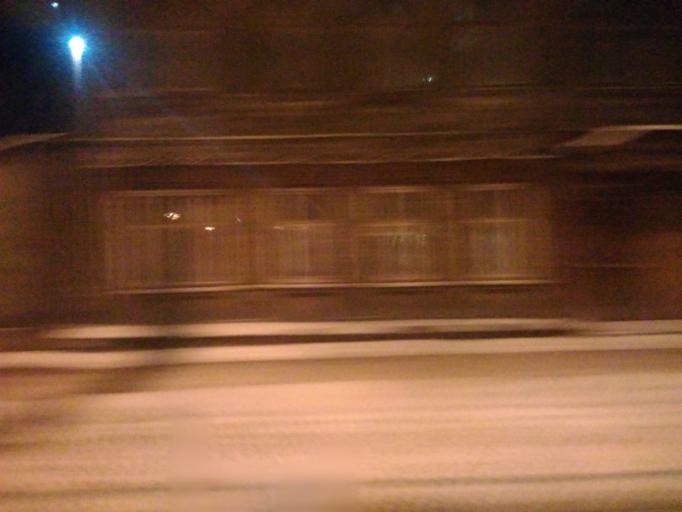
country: RU
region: Ulyanovsk
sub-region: Ulyanovskiy Rayon
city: Ulyanovsk
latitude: 54.3312
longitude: 48.4011
